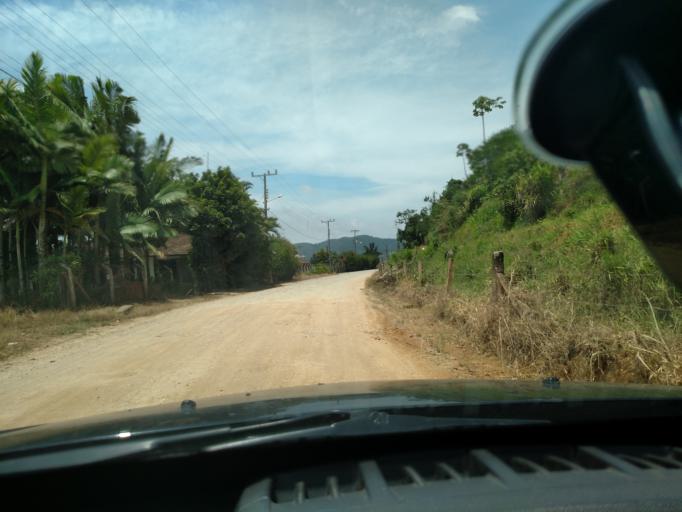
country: BR
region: Santa Catarina
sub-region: Itajai
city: Itajai
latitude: -26.9113
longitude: -48.8044
